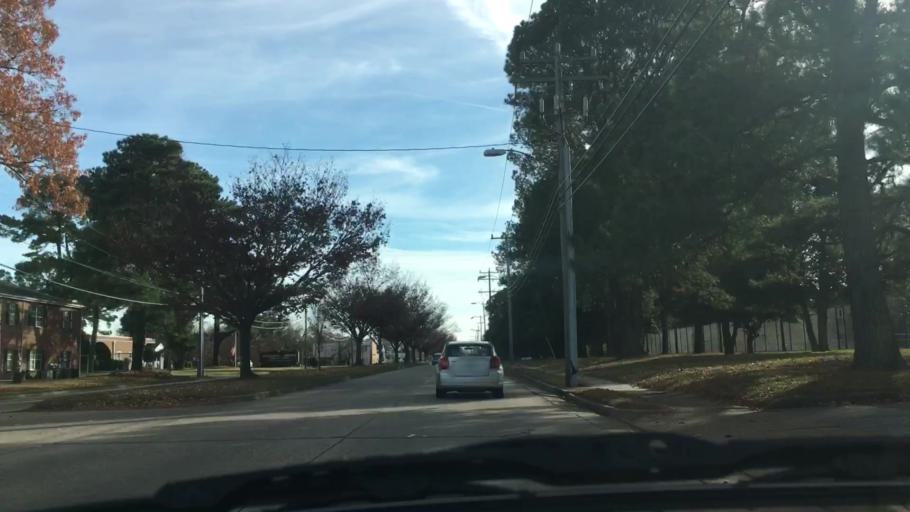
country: US
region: Virginia
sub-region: City of Norfolk
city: Norfolk
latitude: 36.9294
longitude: -76.2533
